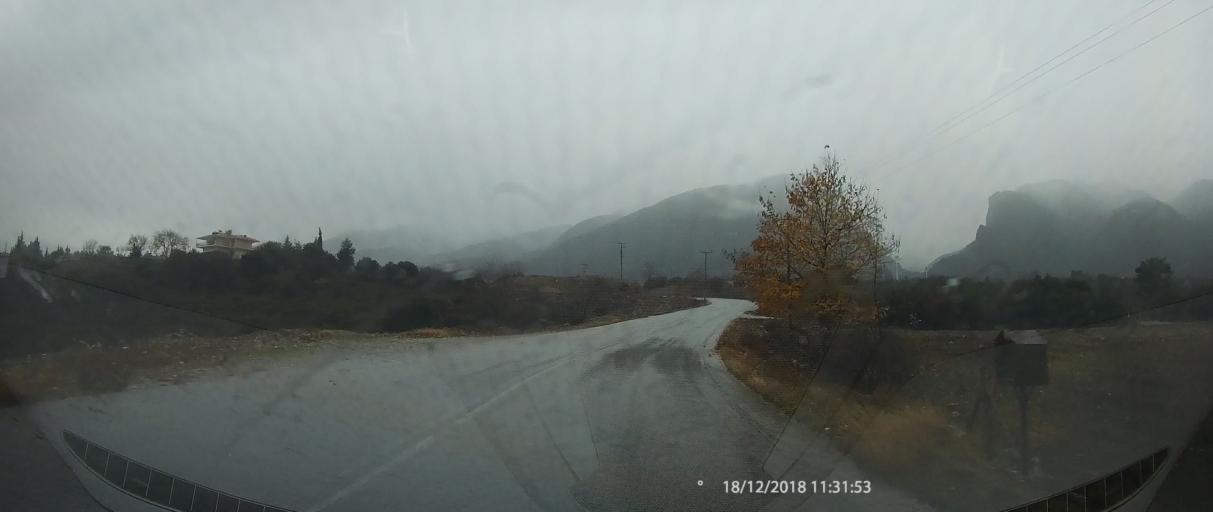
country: GR
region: Central Macedonia
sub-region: Nomos Pierias
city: Litochoro
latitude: 40.1104
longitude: 22.5064
